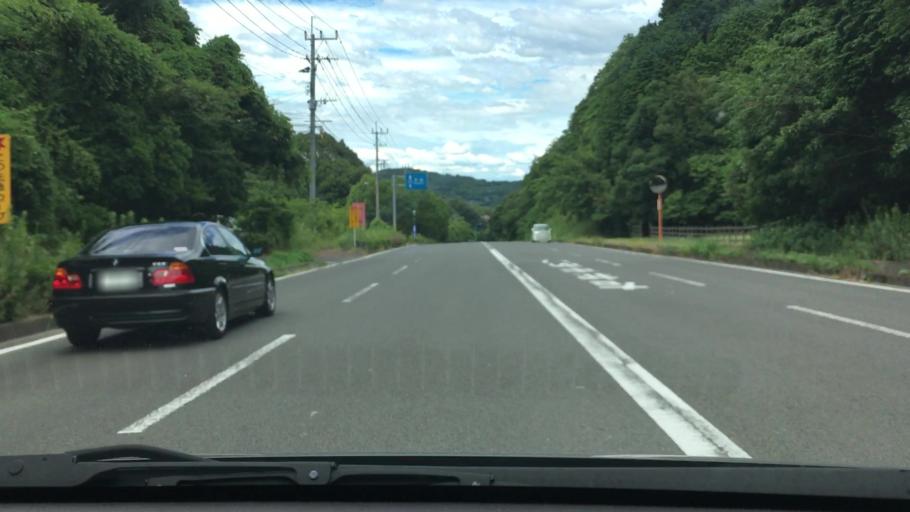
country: JP
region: Nagasaki
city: Sasebo
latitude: 32.9921
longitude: 129.7504
